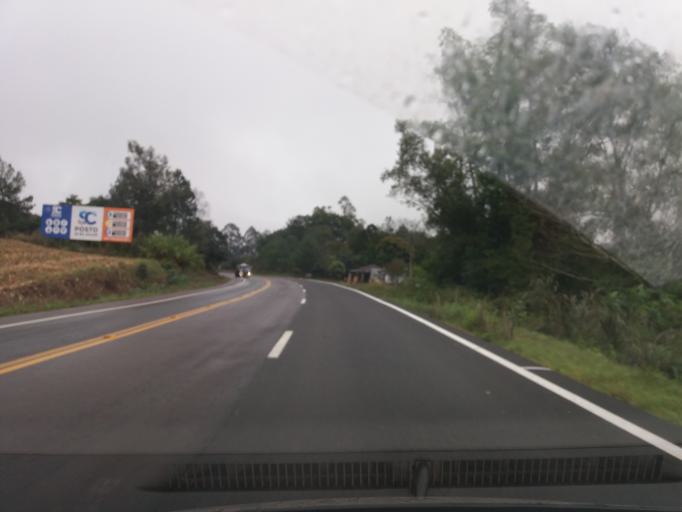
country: BR
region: Parana
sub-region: Realeza
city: Realeza
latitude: -25.5454
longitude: -53.5920
